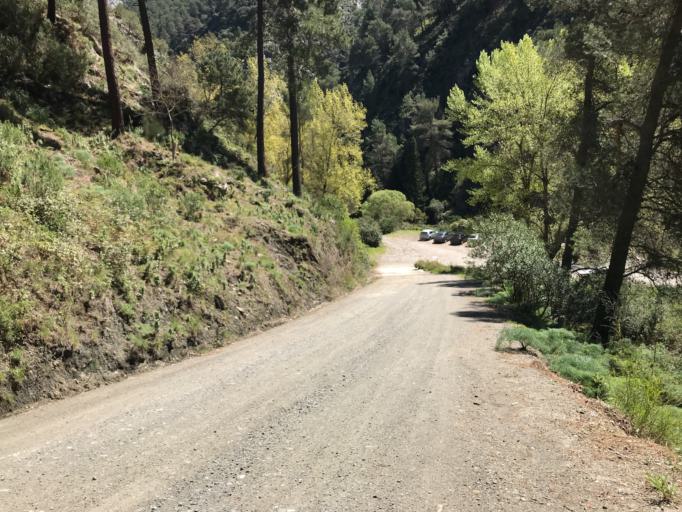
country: ES
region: Andalusia
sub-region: Provincia de Malaga
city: Alcaucin
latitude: 36.9156
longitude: -4.0914
